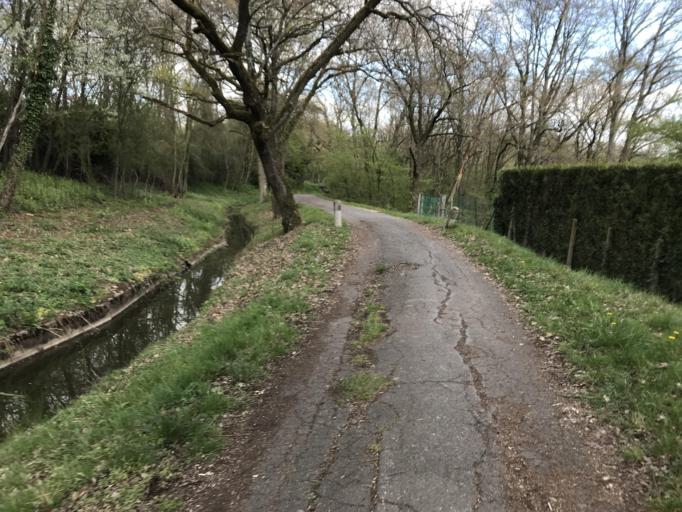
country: FR
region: Ile-de-France
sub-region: Departement de l'Essonne
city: Vauhallan
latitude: 48.7363
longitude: 2.2016
